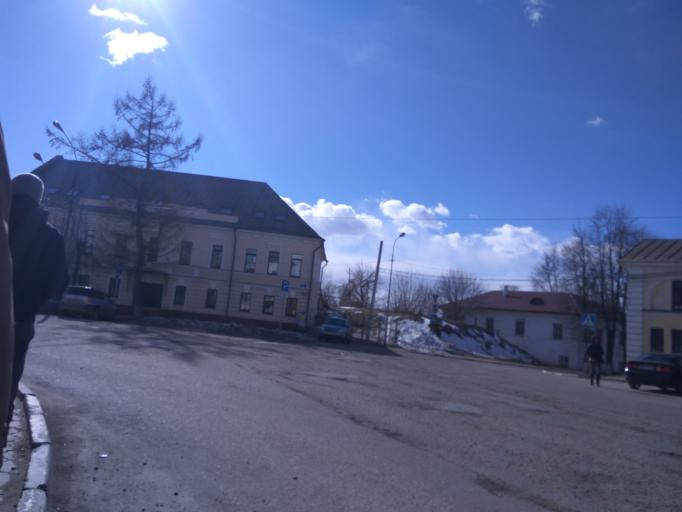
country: RU
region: Jaroslavl
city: Rostov
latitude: 57.1855
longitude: 39.4145
